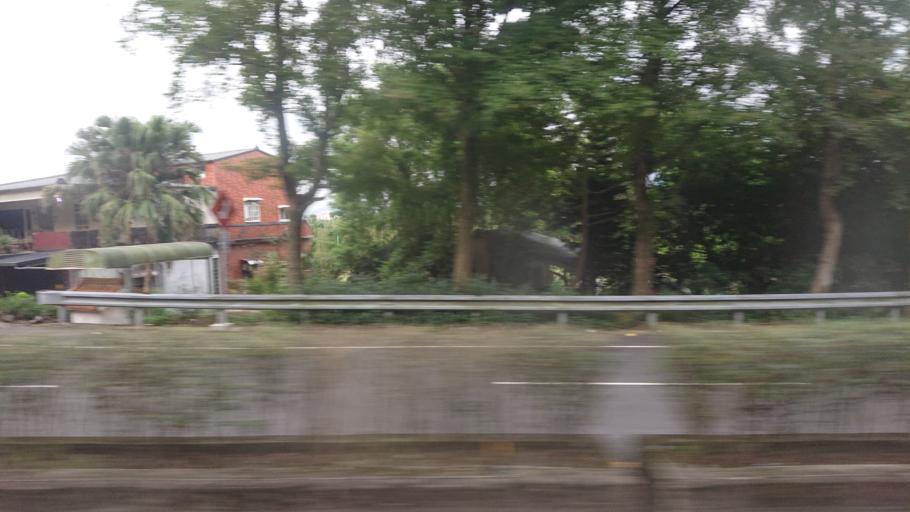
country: TW
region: Taiwan
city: Daxi
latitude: 24.8769
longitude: 121.2500
